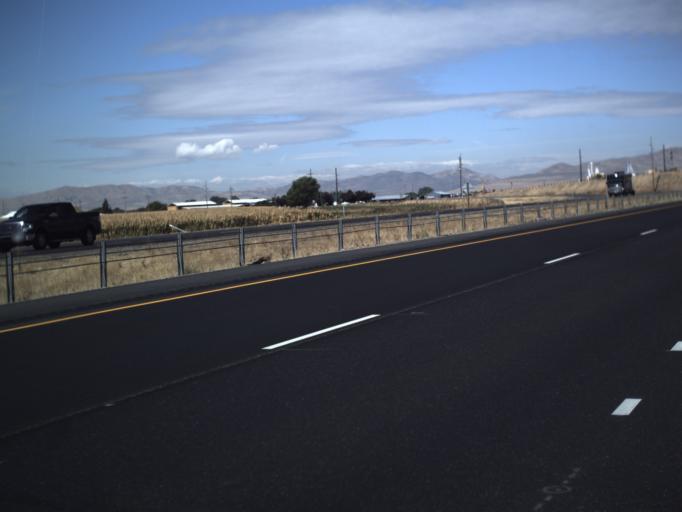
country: US
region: Utah
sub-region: Box Elder County
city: Honeyville
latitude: 41.6314
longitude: -112.0973
